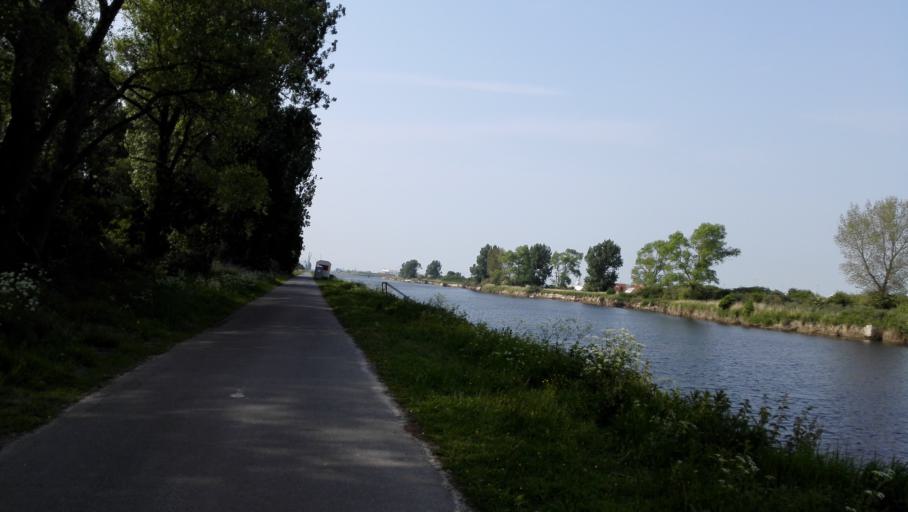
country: BE
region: Flanders
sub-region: Provincie West-Vlaanderen
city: Zeebrugge
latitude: 51.2999
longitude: 3.2047
